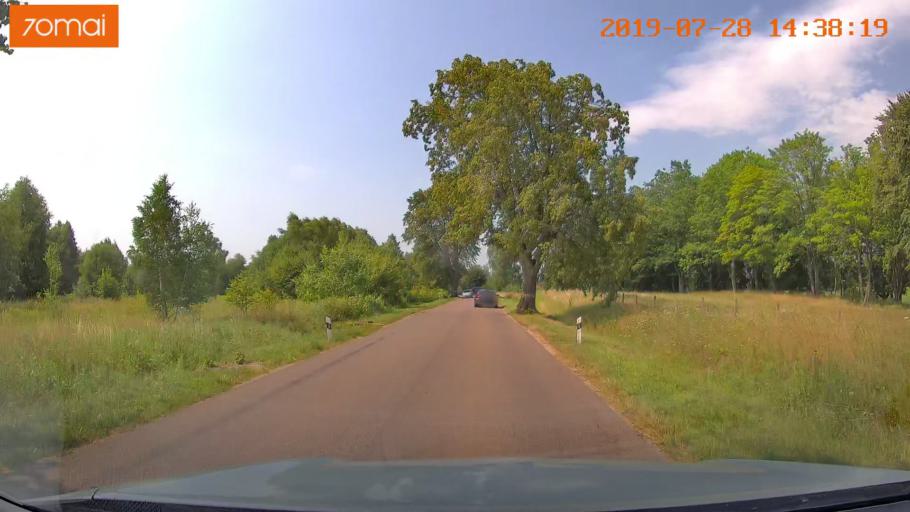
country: RU
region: Kaliningrad
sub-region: Gorod Kaliningrad
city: Yantarnyy
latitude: 54.8442
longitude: 19.9856
